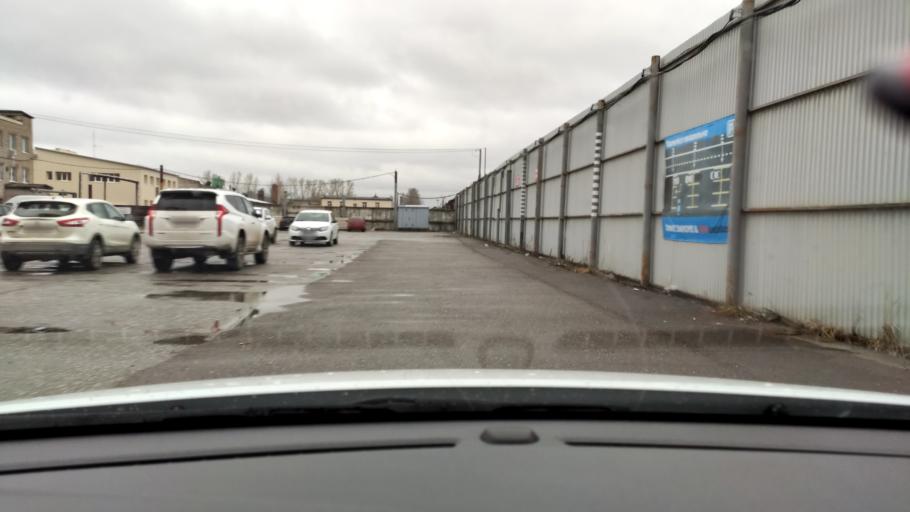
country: RU
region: Tatarstan
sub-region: Gorod Kazan'
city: Kazan
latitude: 55.7361
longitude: 49.1360
